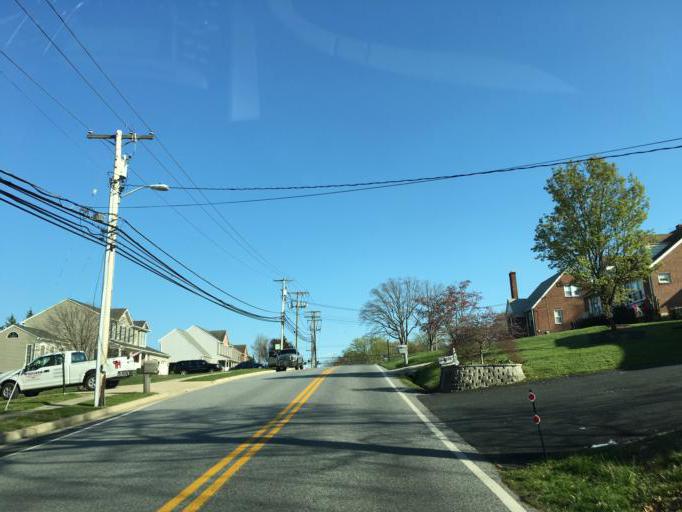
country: US
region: Maryland
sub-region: Baltimore County
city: Perry Hall
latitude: 39.3988
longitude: -76.4872
